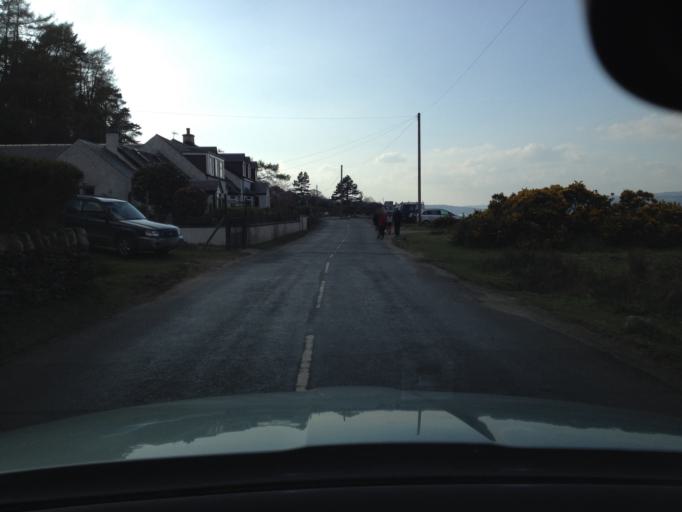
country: GB
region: Scotland
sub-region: North Ayrshire
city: Isle of Arran
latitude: 55.7044
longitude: -5.2931
